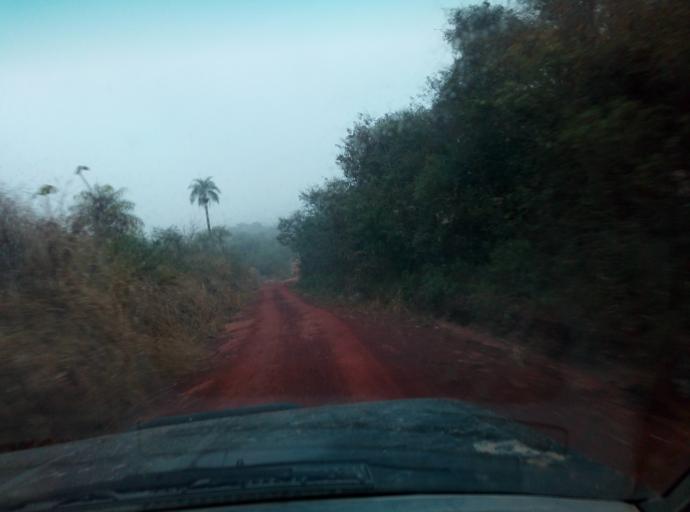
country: PY
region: Caaguazu
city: Doctor Cecilio Baez
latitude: -25.1586
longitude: -56.2553
